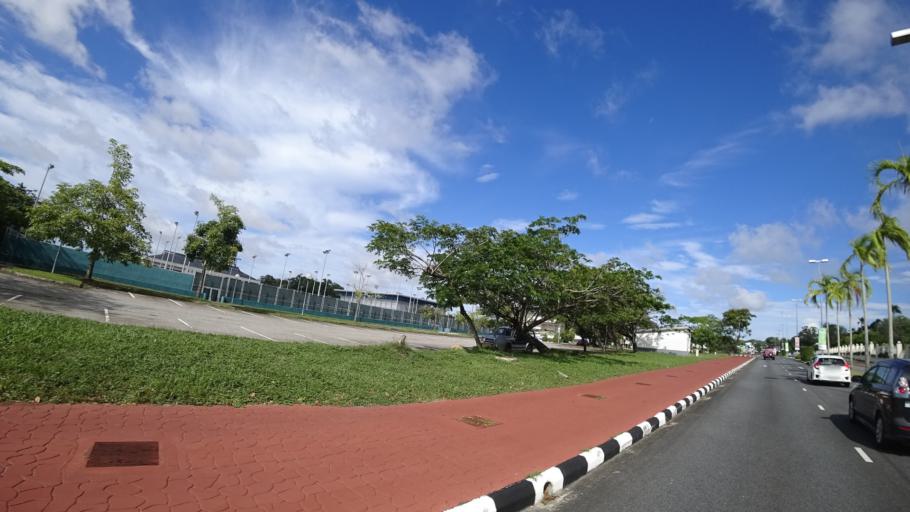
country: BN
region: Brunei and Muara
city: Bandar Seri Begawan
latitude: 4.9269
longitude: 114.9467
